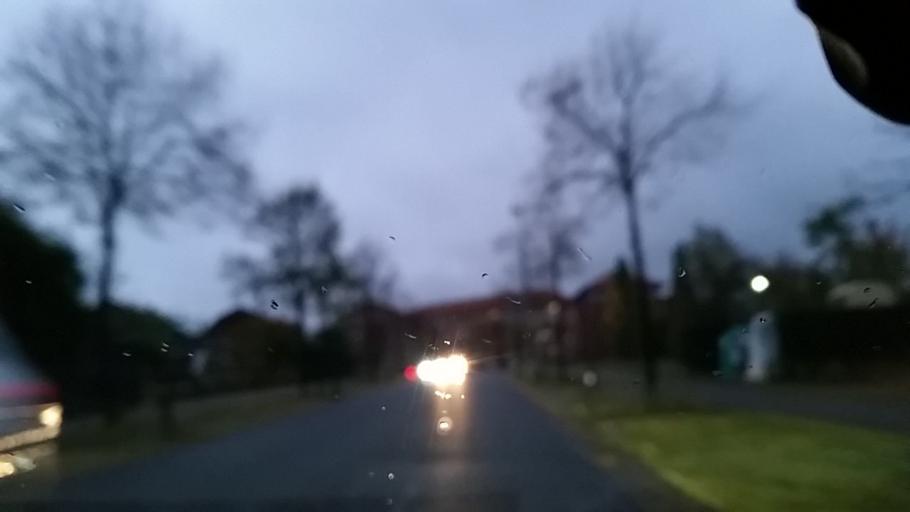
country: DE
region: Lower Saxony
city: Wolfsburg
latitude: 52.4168
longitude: 10.8318
